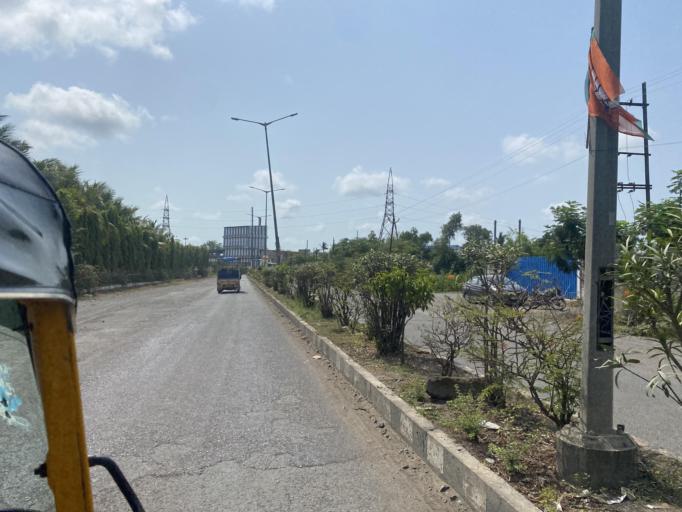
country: IN
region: Gujarat
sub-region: Valsad
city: Vapi
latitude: 20.2843
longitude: 72.8567
